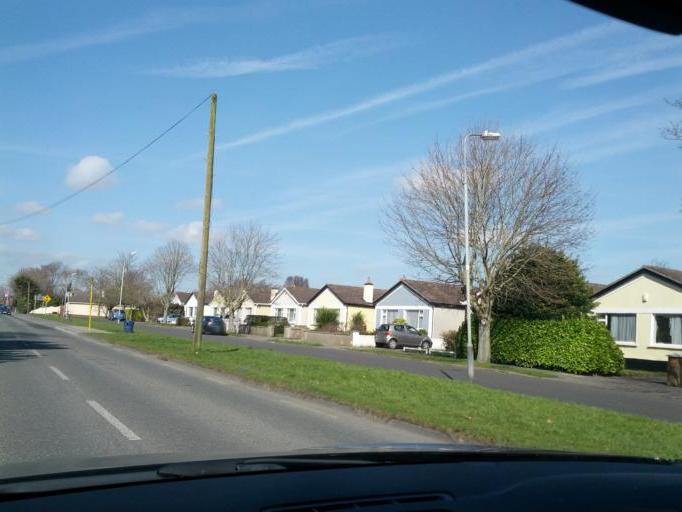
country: IE
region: Leinster
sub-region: Kildare
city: Maynooth
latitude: 53.3737
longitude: -6.5860
